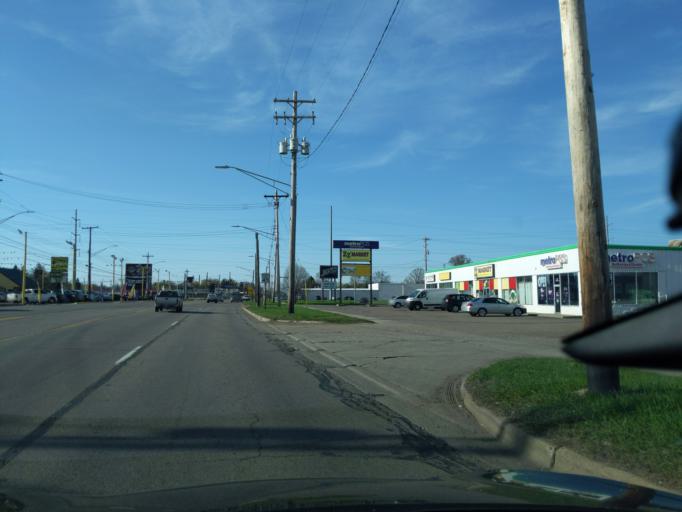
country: US
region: Michigan
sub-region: Ingham County
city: Holt
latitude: 42.6771
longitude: -84.5478
